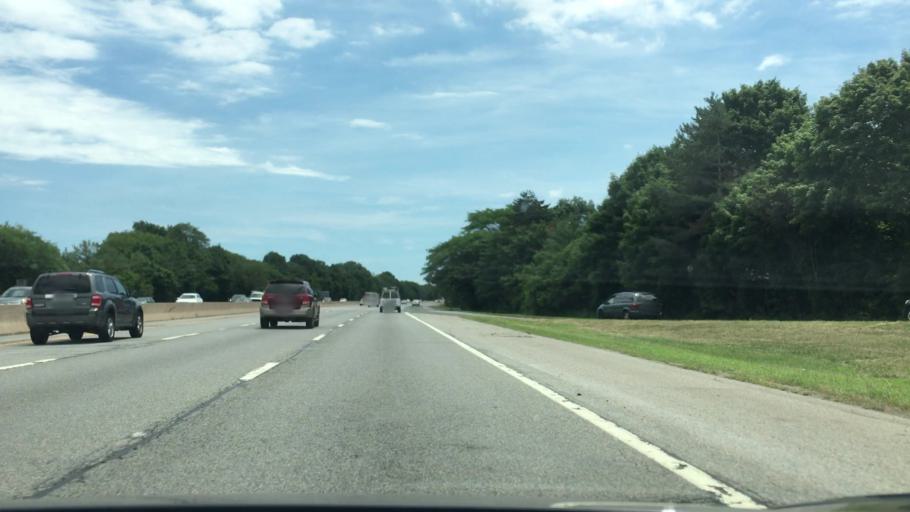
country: US
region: New York
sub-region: Nassau County
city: Plainview
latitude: 40.7726
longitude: -73.4808
